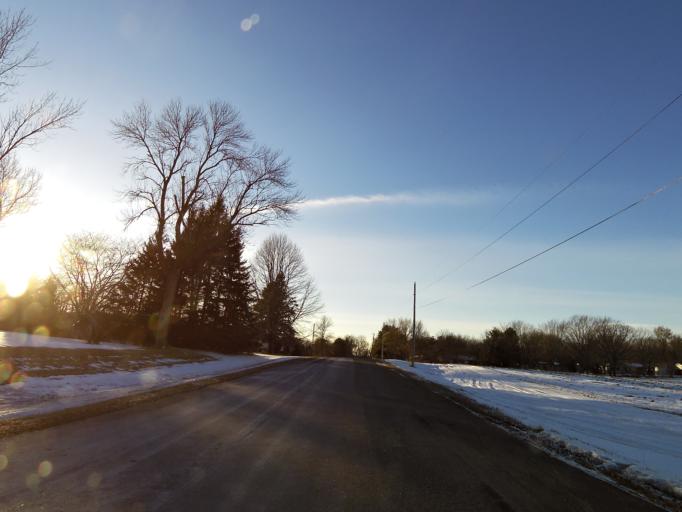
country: US
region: Minnesota
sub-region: Washington County
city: Cottage Grove
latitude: 44.8371
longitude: -92.8760
